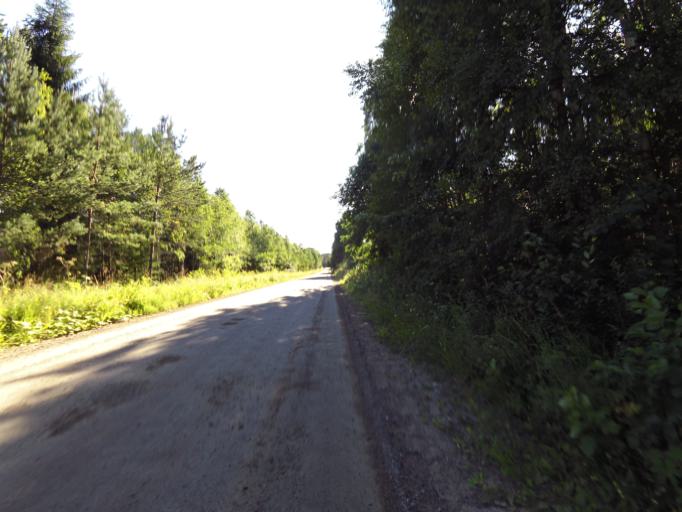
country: SE
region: Gaevleborg
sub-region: Hofors Kommun
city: Hofors
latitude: 60.5925
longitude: 16.2650
